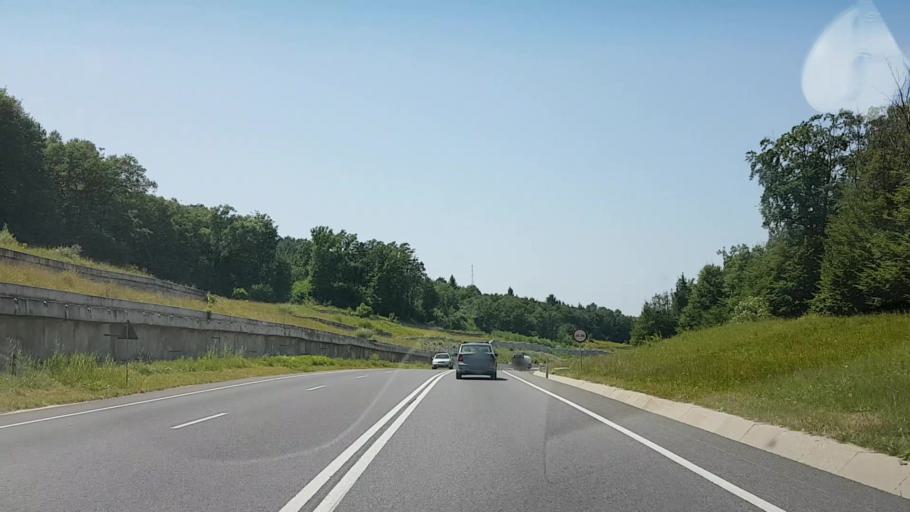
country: RO
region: Cluj
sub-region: Comuna Feleacu
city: Gheorghieni
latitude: 46.7192
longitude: 23.6553
